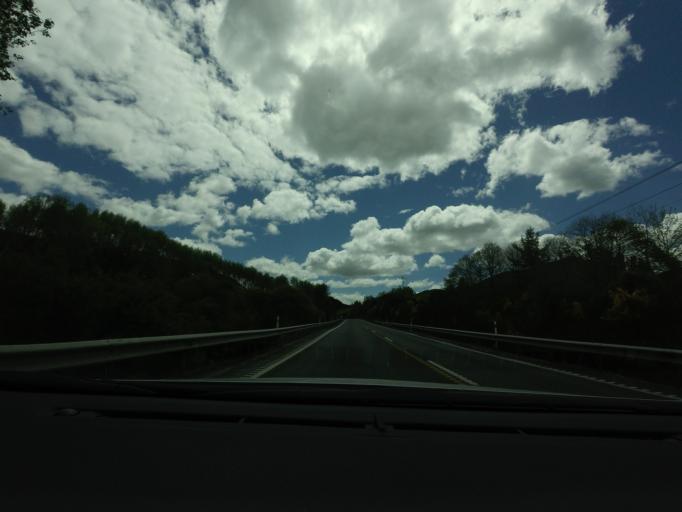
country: NZ
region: Bay of Plenty
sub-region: Rotorua District
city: Rotorua
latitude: -38.2984
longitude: 176.3616
